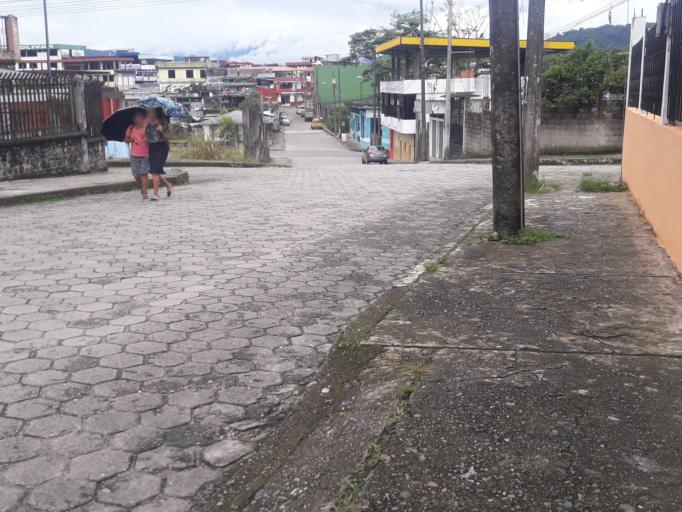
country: EC
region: Napo
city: Tena
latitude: -0.9967
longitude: -77.8107
